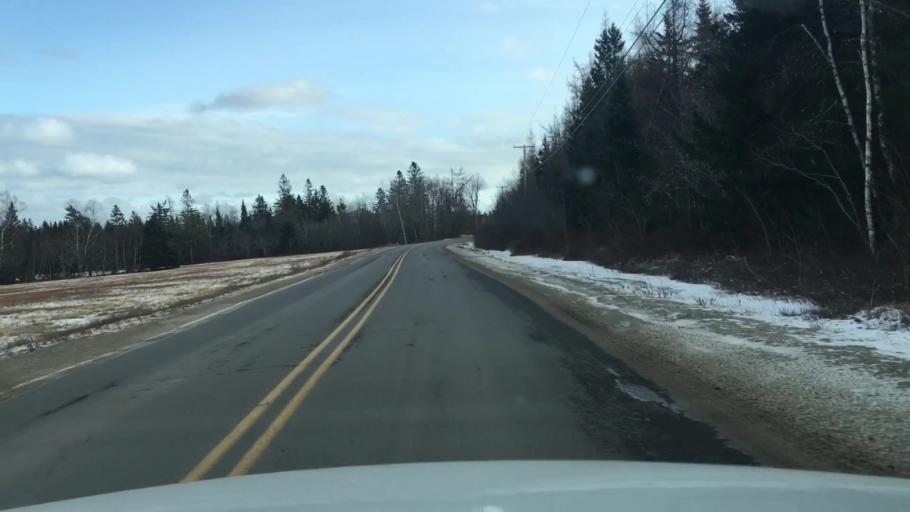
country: US
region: Maine
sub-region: Washington County
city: Jonesport
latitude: 44.6157
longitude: -67.6056
